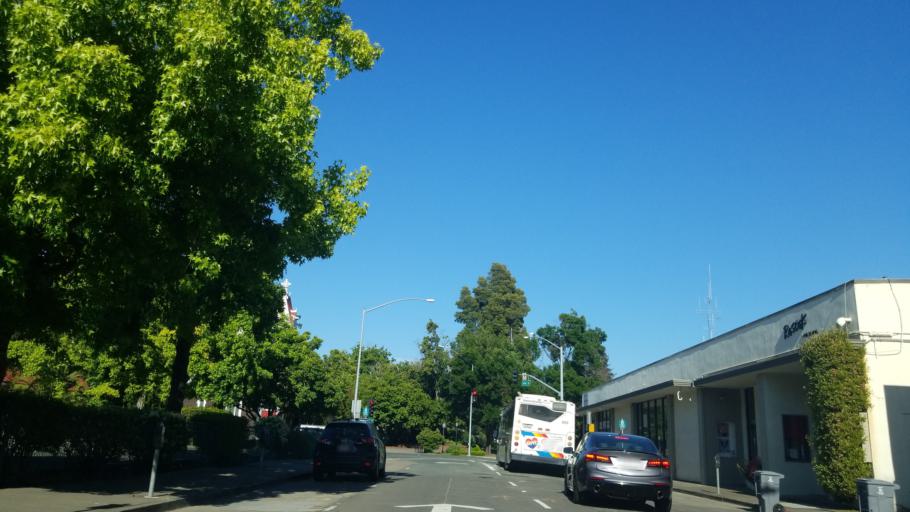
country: US
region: California
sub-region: Sonoma County
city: Santa Rosa
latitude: 38.4439
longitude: -122.7173
